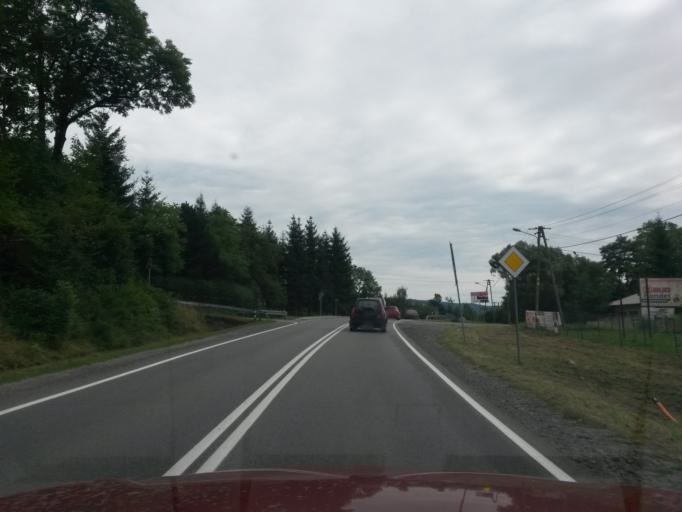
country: PL
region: Lesser Poland Voivodeship
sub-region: Powiat nowosadecki
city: Labowa
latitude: 49.5314
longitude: 20.8483
